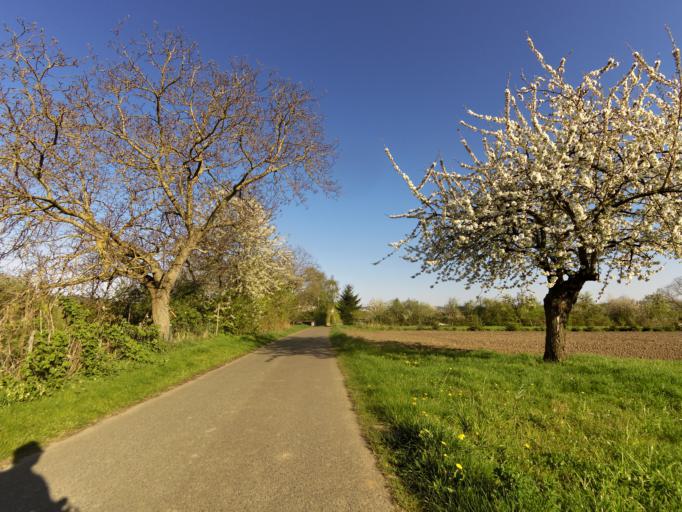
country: DE
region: Rheinland-Pfalz
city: Weitersburg
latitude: 50.4006
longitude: 7.5976
